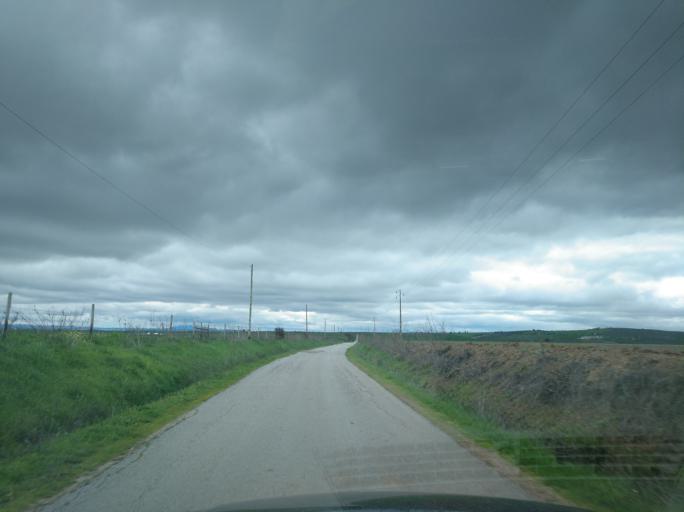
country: PT
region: Portalegre
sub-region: Elvas
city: Elvas
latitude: 38.9313
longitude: -7.0931
